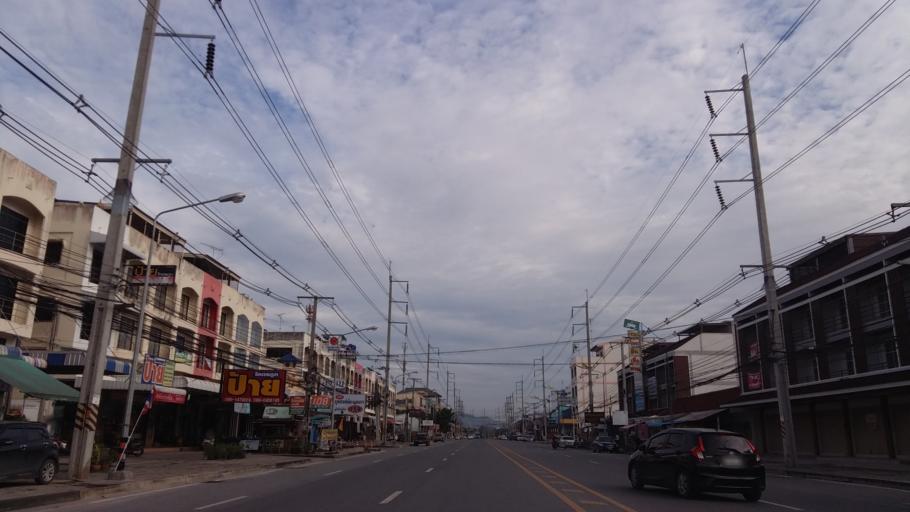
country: TH
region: Chon Buri
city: Chon Buri
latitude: 13.3224
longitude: 100.9450
